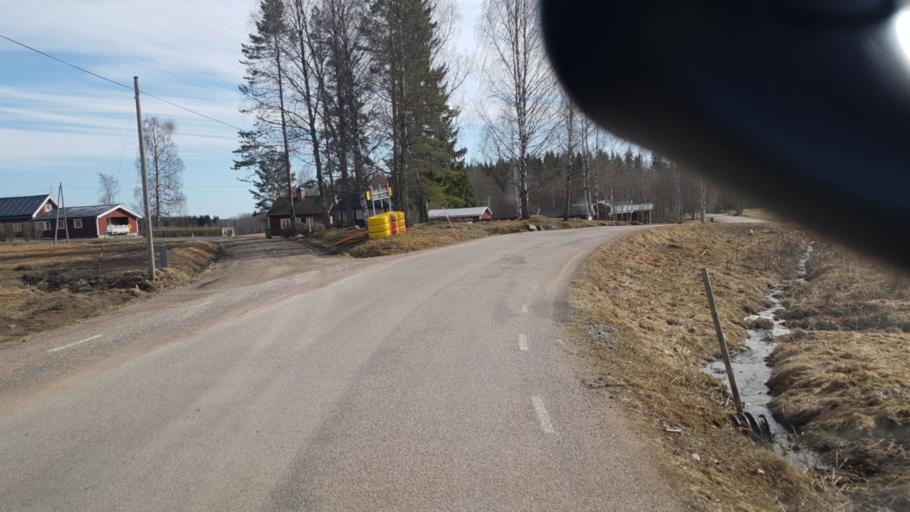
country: SE
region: Vaermland
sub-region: Eda Kommun
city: Charlottenberg
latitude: 59.8627
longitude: 12.3451
